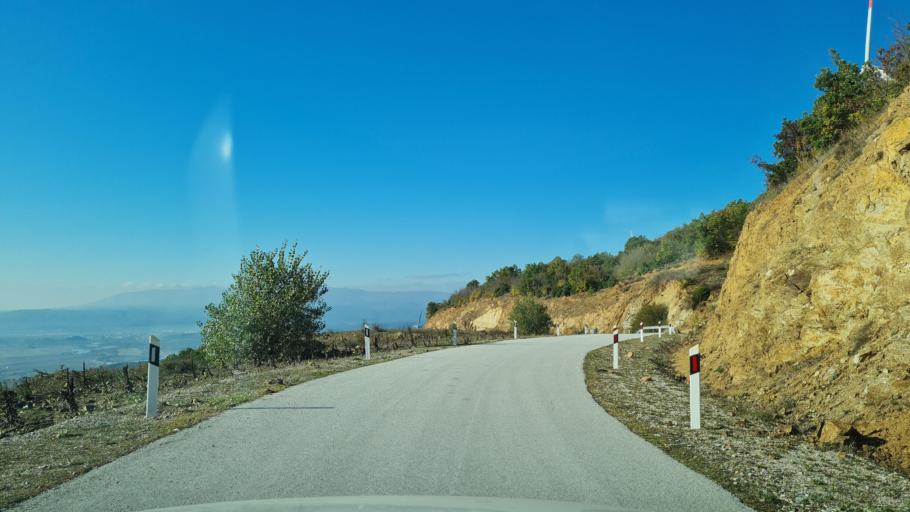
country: MK
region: Bogdanci
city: Bogdanci
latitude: 41.2263
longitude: 22.5620
